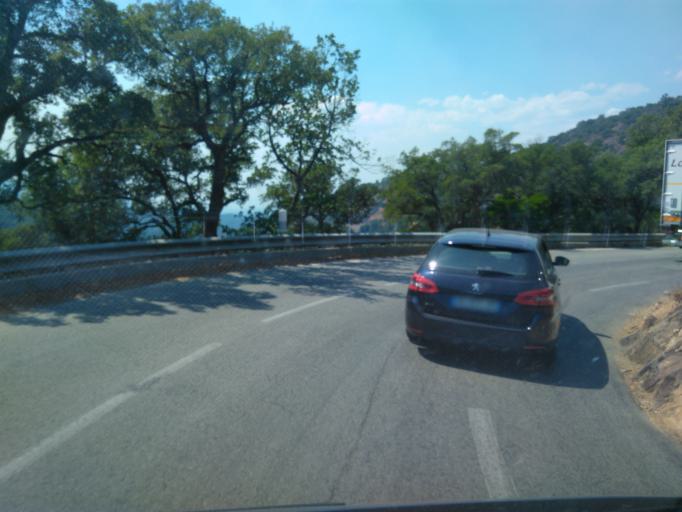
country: FR
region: Provence-Alpes-Cote d'Azur
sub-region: Departement du Var
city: La Garde-Freinet
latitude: 43.3305
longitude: 6.4582
